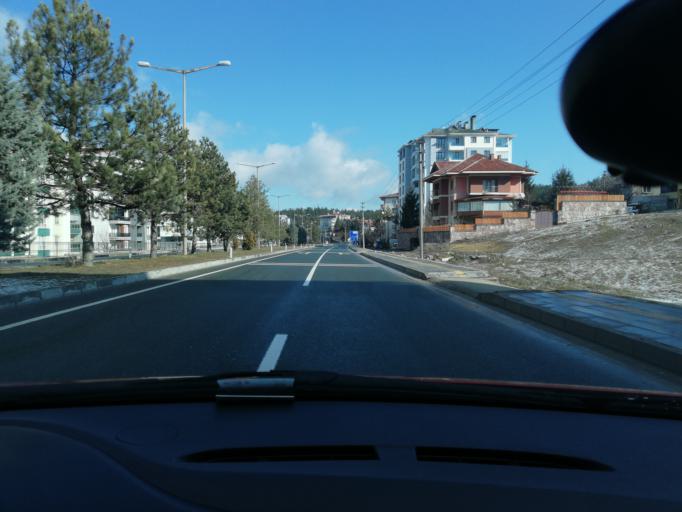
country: TR
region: Kastamonu
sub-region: Cide
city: Kastamonu
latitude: 41.3552
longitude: 33.7679
